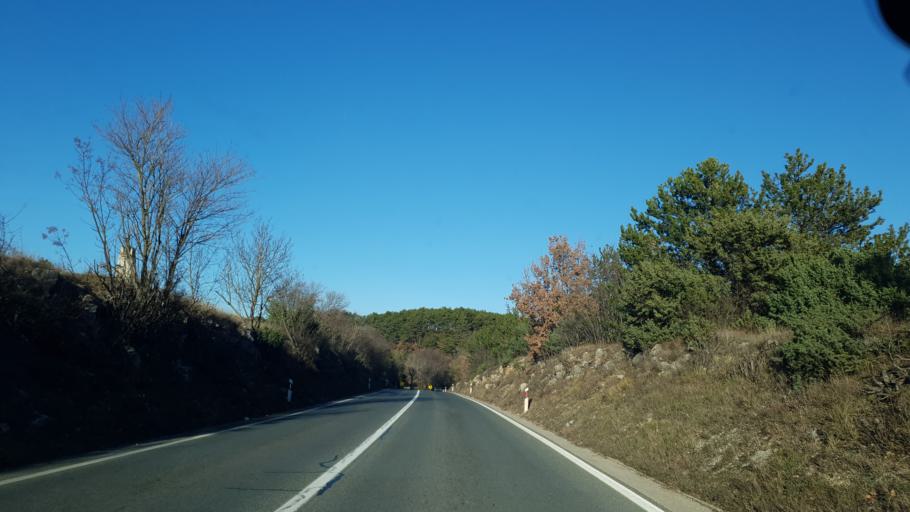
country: HR
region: Splitsko-Dalmatinska
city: Brnaze
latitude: 43.6642
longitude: 16.6462
